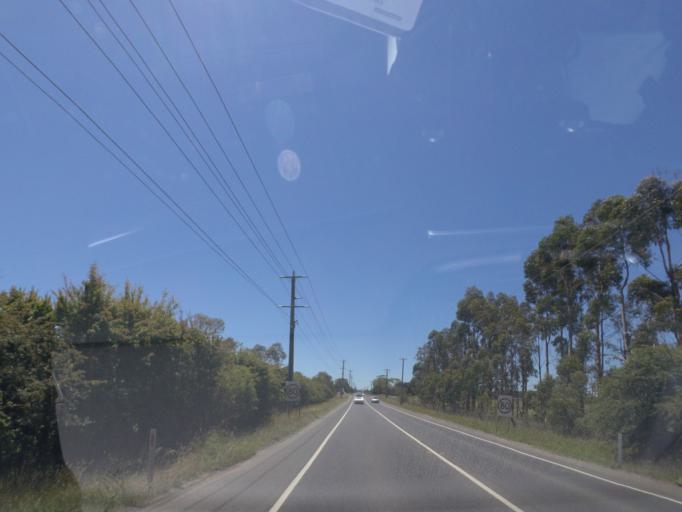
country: AU
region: Victoria
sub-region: Whittlesea
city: Epping
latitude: -37.6018
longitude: 145.0325
